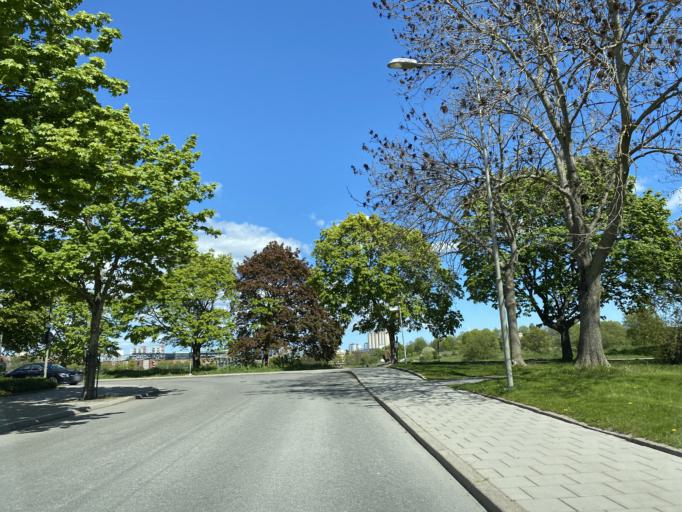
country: SE
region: Stockholm
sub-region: Stockholms Kommun
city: OEstermalm
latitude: 59.3355
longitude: 18.1070
